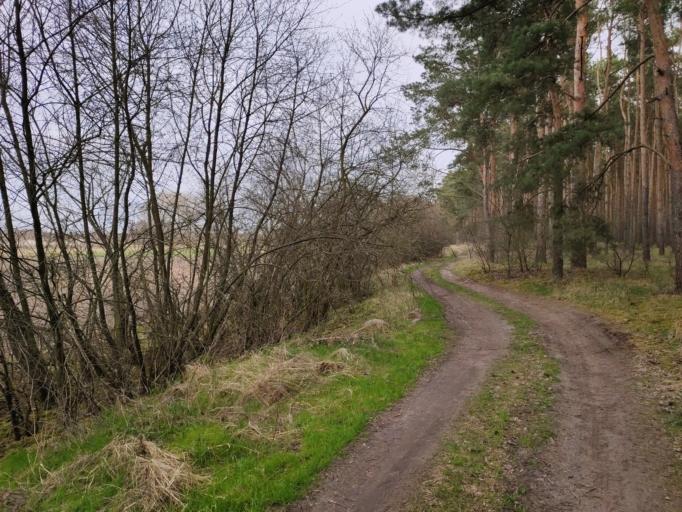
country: PL
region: Greater Poland Voivodeship
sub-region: Powiat sredzki
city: Sroda Wielkopolska
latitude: 52.1474
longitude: 17.2816
